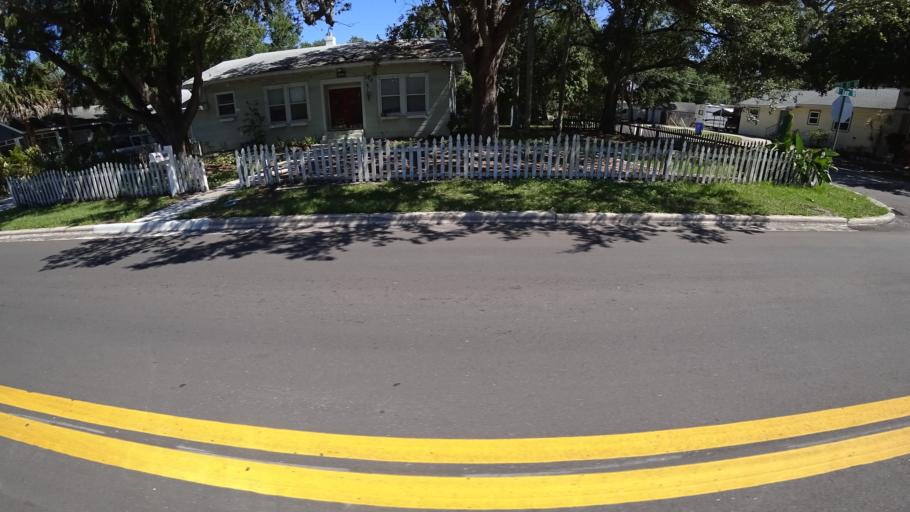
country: US
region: Florida
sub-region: Manatee County
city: Bradenton
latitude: 27.4920
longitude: -82.5905
